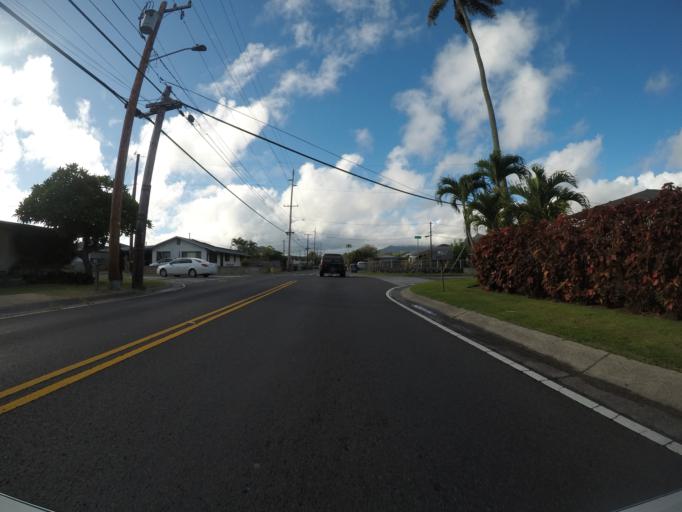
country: US
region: Hawaii
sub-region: Honolulu County
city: Kailua
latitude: 21.4047
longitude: -157.7505
